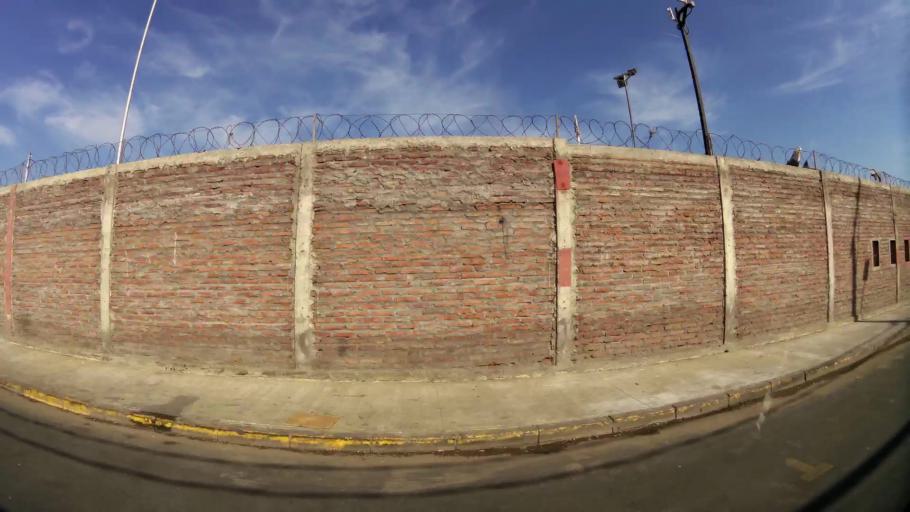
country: CL
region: Santiago Metropolitan
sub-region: Provincia de Santiago
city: Santiago
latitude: -33.4038
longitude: -70.6575
